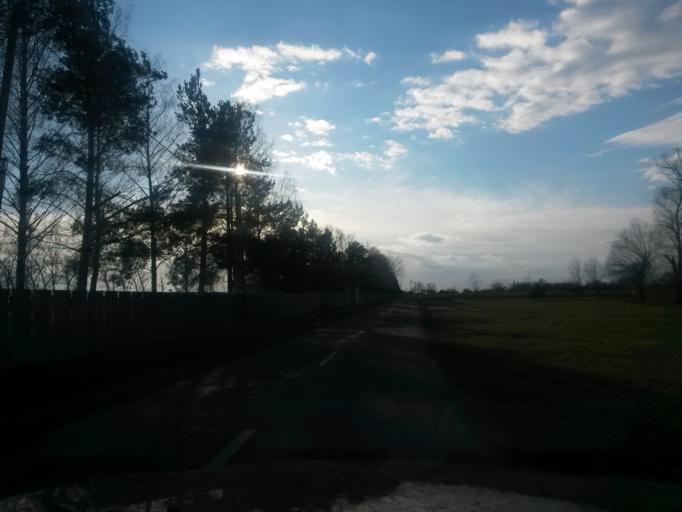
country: SK
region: Kosicky
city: Sobrance
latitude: 48.7404
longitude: 22.0880
